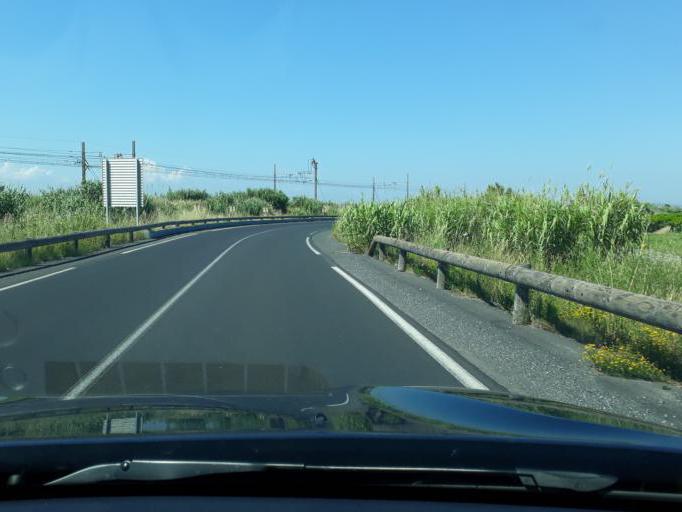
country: FR
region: Languedoc-Roussillon
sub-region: Departement de l'Herault
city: Marseillan
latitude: 43.3420
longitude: 3.5776
